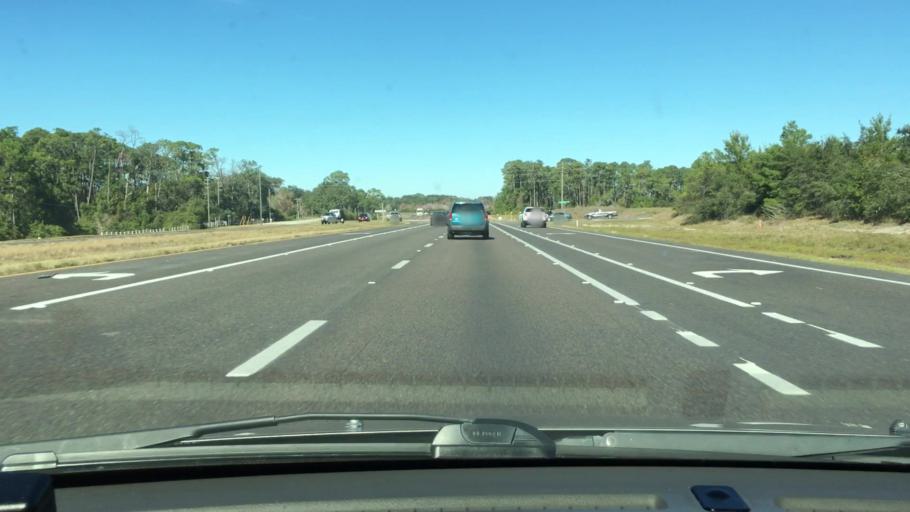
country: US
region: Florida
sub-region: Osceola County
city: Saint Cloud
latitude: 28.2270
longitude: -81.1831
